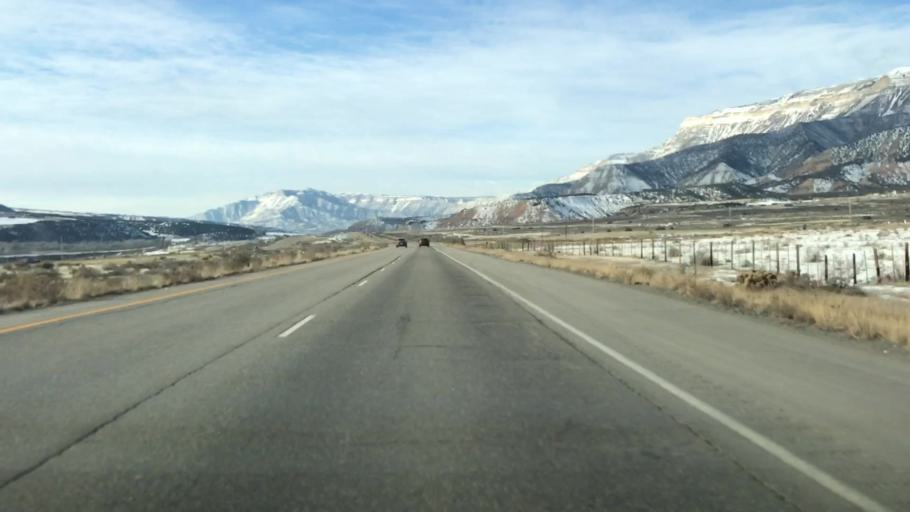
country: US
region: Colorado
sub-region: Garfield County
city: Rifle
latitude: 39.5055
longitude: -107.8928
